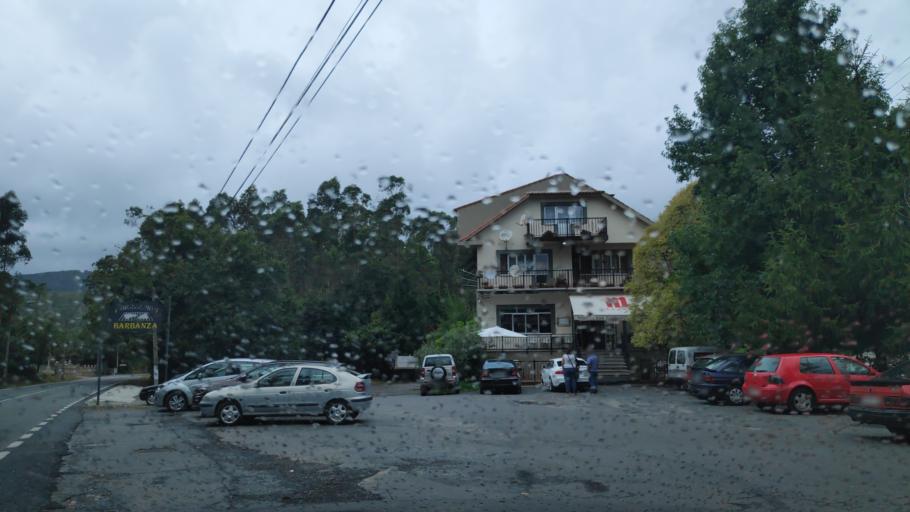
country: ES
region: Galicia
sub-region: Provincia de Pontevedra
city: Catoira
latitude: 42.6934
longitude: -8.7748
